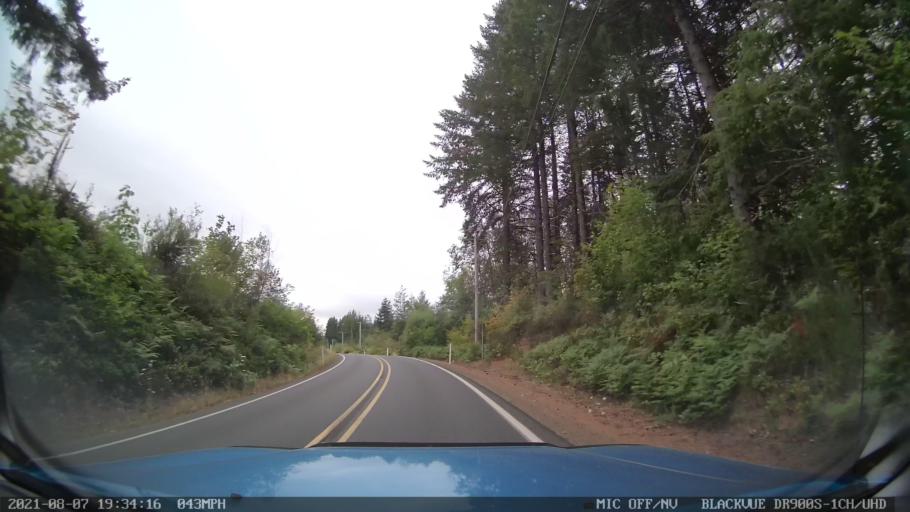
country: US
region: Oregon
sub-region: Linn County
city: Lyons
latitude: 44.9156
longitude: -122.6548
